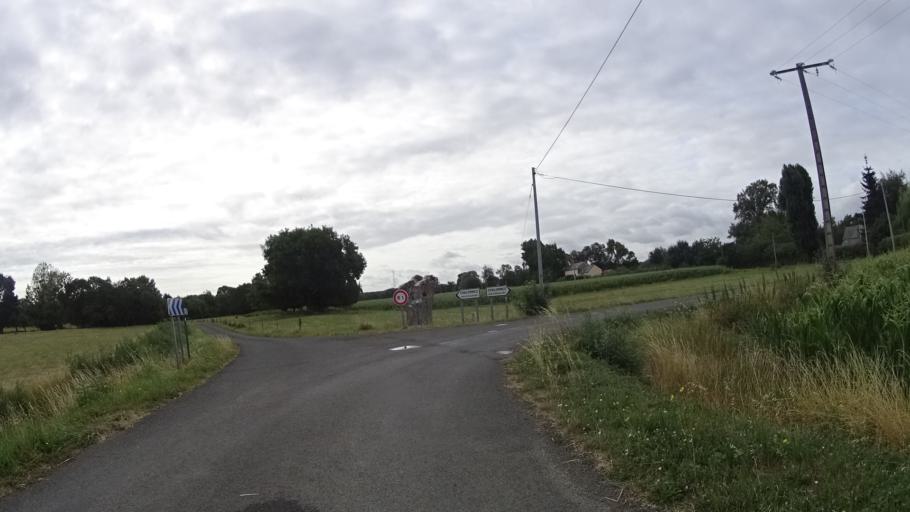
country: FR
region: Pays de la Loire
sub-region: Departement de Maine-et-Loire
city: Montjean-sur-Loire
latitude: 47.3861
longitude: -0.8393
